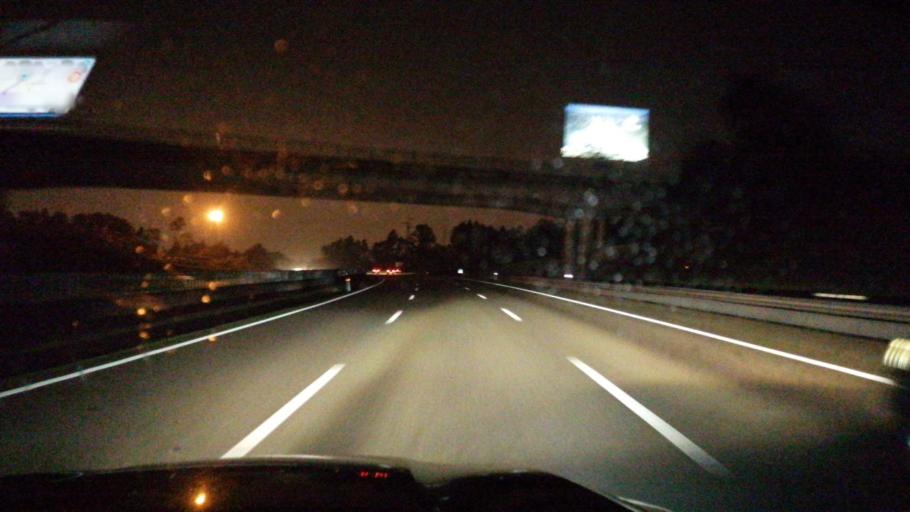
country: PT
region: Aveiro
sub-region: Santa Maria da Feira
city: Rio Meao
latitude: 40.9627
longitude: -8.5672
